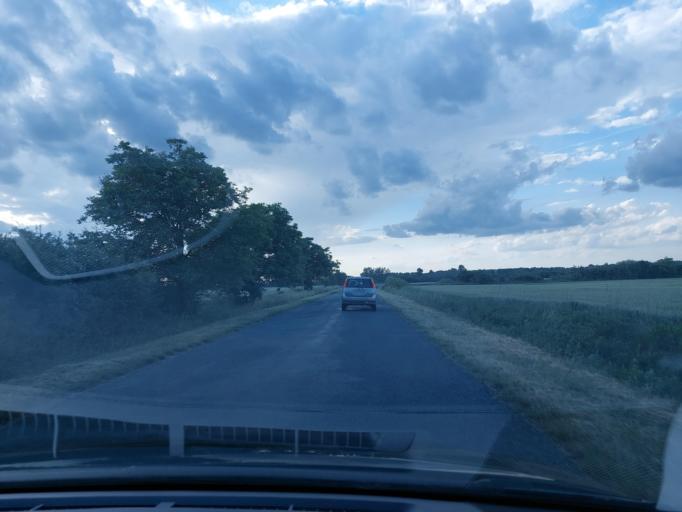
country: HU
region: Veszprem
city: Devecser
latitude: 47.1825
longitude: 17.3607
